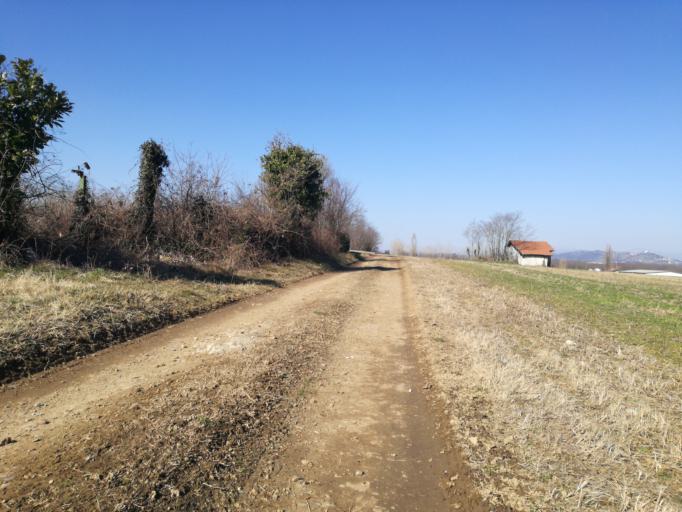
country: IT
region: Lombardy
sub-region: Provincia di Lecco
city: Verderio Inferiore
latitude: 45.6537
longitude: 9.4334
